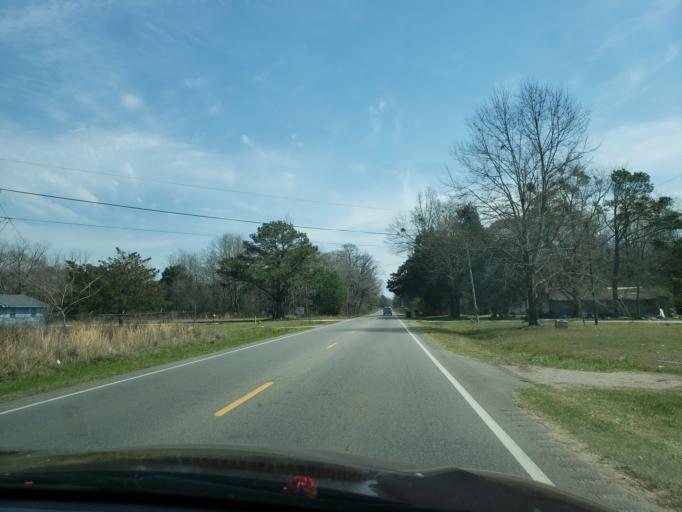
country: US
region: Alabama
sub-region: Autauga County
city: Prattville
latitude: 32.4309
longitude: -86.4987
